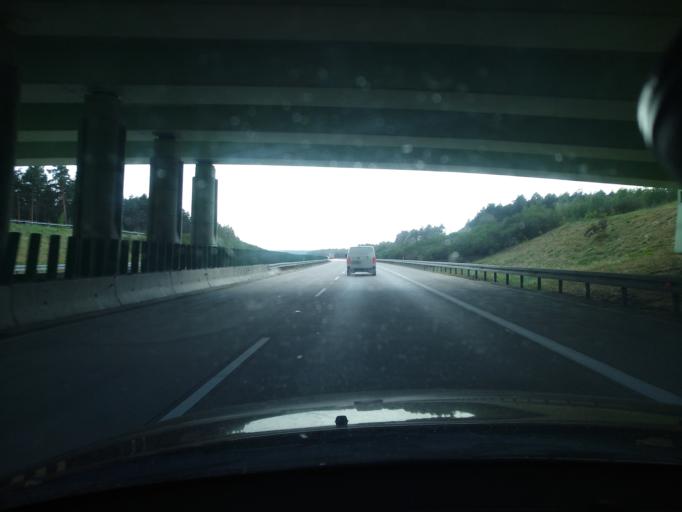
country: PL
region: Lower Silesian Voivodeship
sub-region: Powiat boleslawiecki
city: Nowogrodziec
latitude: 51.2649
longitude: 15.3695
